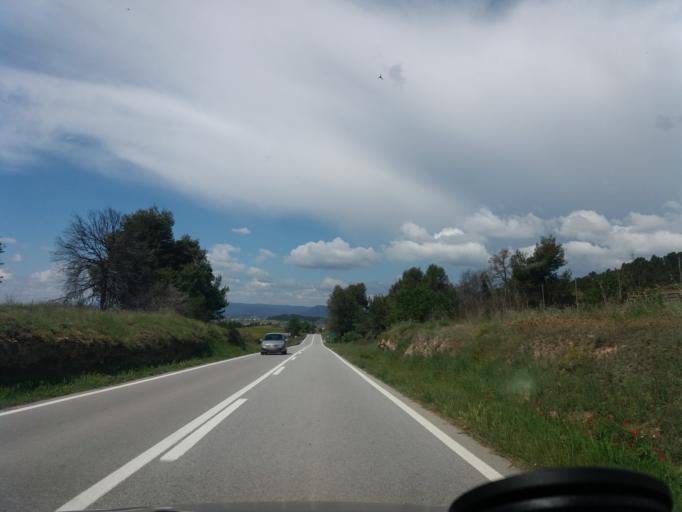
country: ES
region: Catalonia
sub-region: Provincia de Barcelona
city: Navarcles
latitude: 41.7654
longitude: 1.9190
